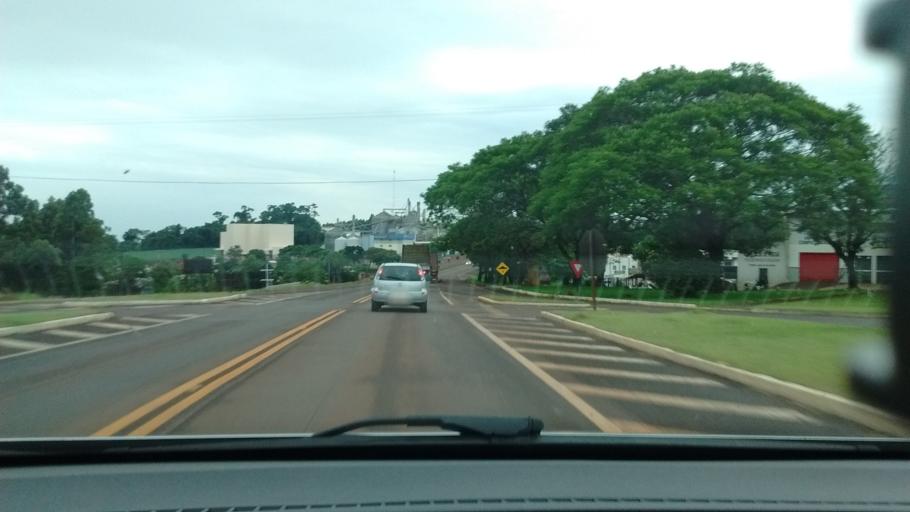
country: BR
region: Parana
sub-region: Corbelia
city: Corbelia
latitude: -24.7930
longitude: -53.2884
